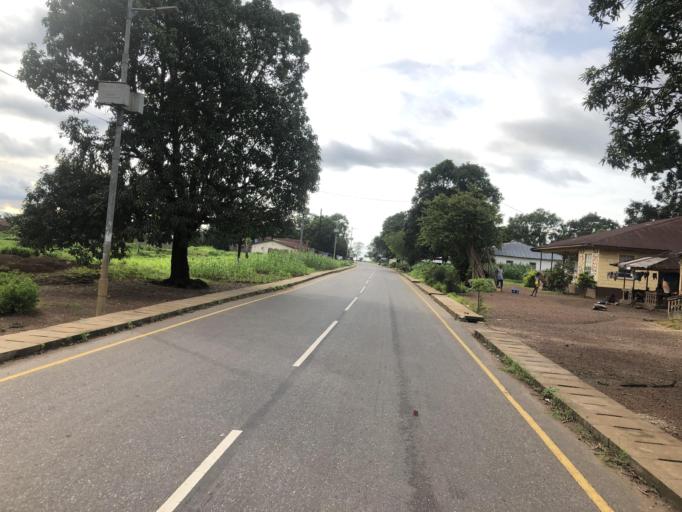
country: SL
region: Northern Province
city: Port Loko
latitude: 8.7736
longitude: -12.7925
